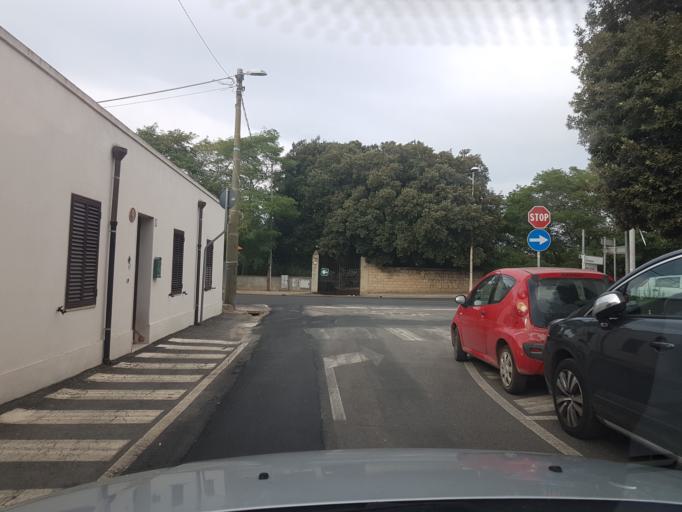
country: IT
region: Sardinia
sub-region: Provincia di Oristano
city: Donigala Fenugheddu
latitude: 39.9276
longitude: 8.5765
